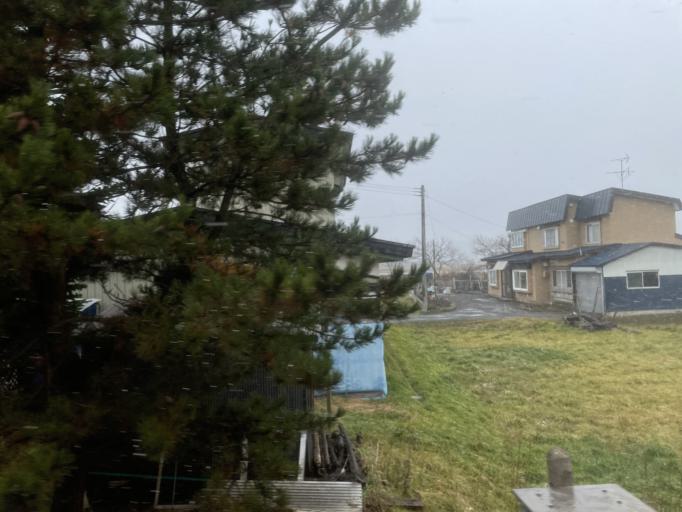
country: JP
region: Aomori
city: Aomori Shi
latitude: 40.8983
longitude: 140.6730
